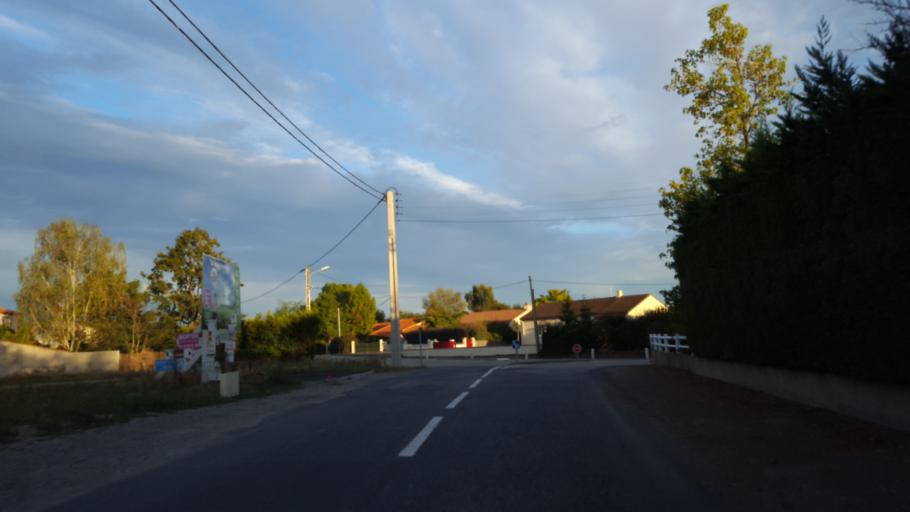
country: FR
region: Pays de la Loire
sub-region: Departement de la Loire-Atlantique
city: Basse-Goulaine
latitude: 47.2084
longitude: -1.4743
